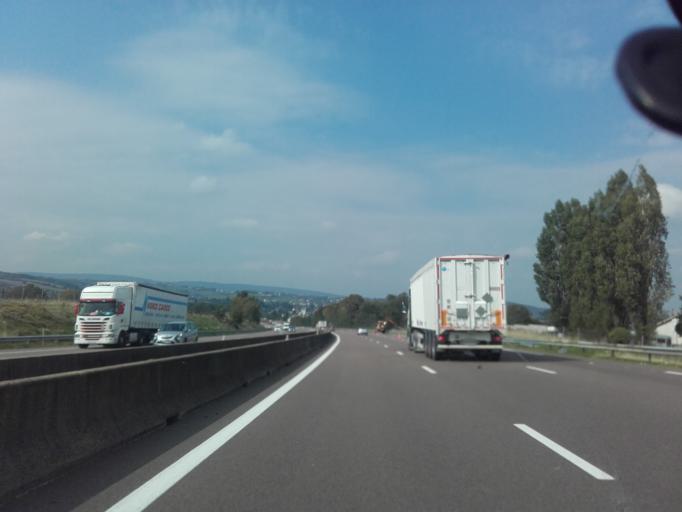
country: FR
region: Bourgogne
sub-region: Departement de Saone-et-Loire
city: Tournus
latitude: 46.5453
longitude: 4.9162
